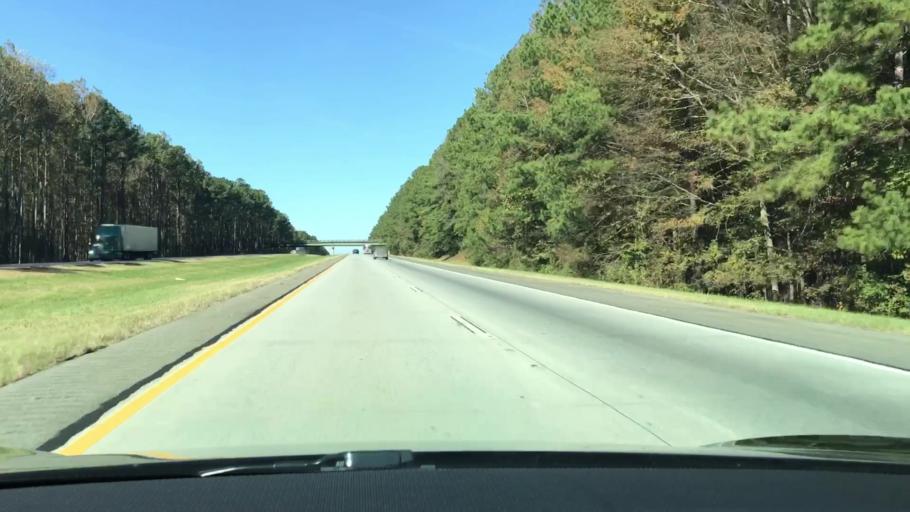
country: US
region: Georgia
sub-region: Taliaferro County
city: Crawfordville
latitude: 33.5100
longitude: -82.8428
